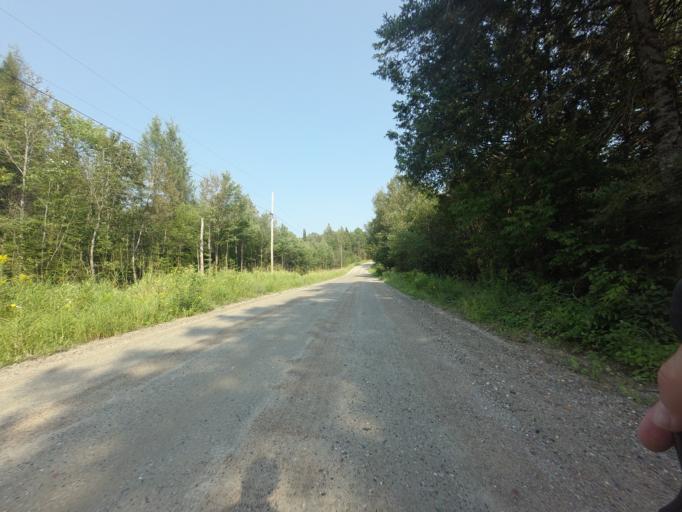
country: CA
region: Ontario
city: Skatepark
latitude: 44.7834
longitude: -76.7973
